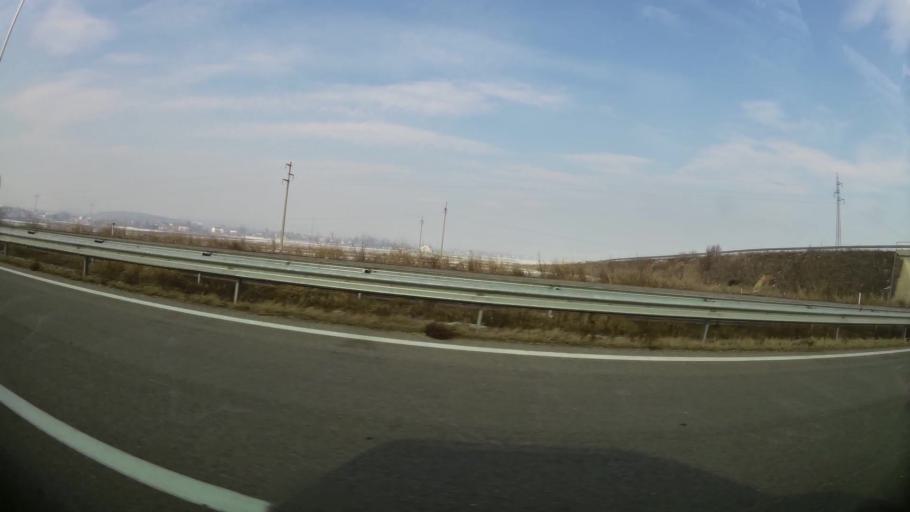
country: MK
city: Creshevo
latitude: 42.0323
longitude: 21.4981
